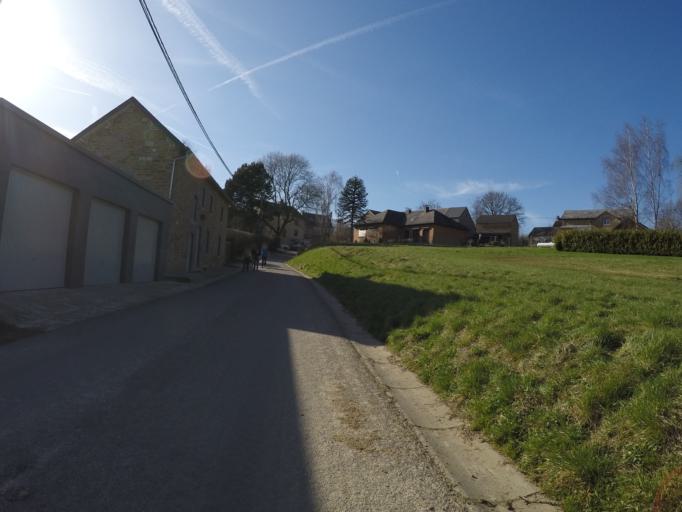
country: BE
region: Wallonia
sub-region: Province de Namur
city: Hamois
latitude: 50.3482
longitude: 5.1168
